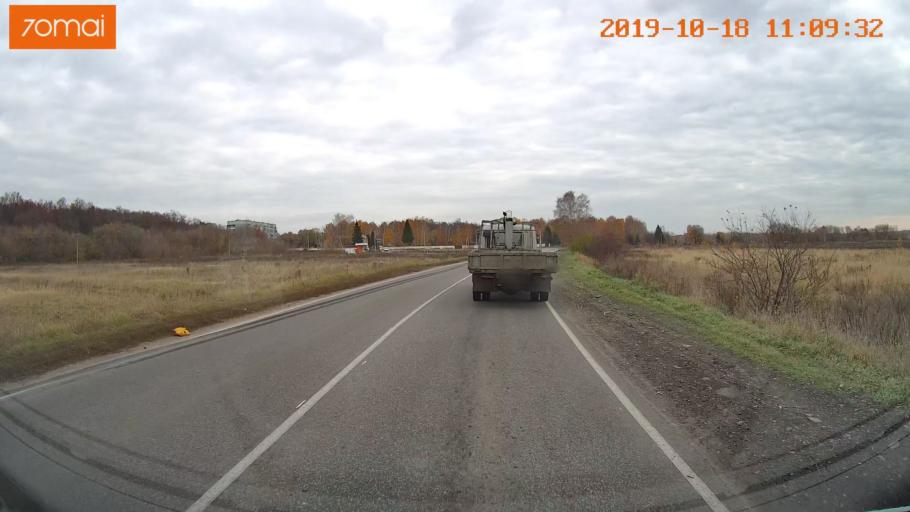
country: RU
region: Tula
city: Kimovsk
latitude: 53.9517
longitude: 38.5366
